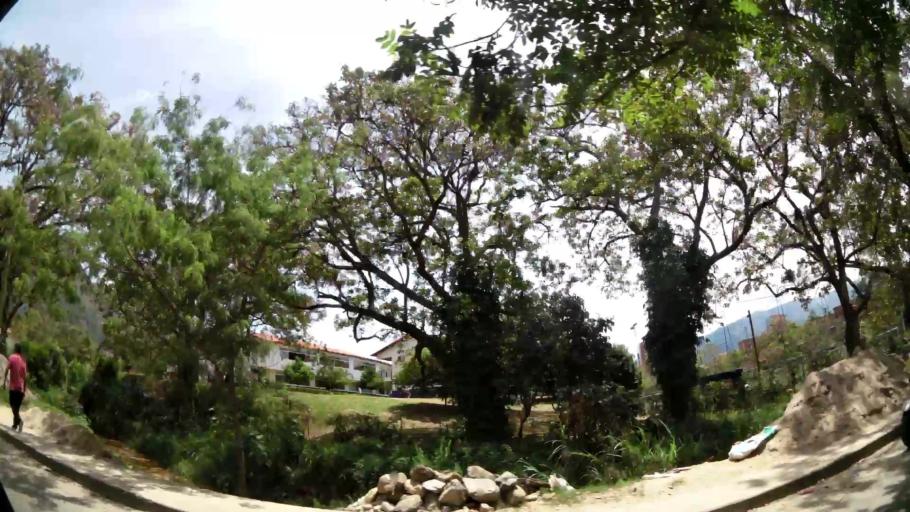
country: CO
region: Antioquia
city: Bello
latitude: 6.3440
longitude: -75.5698
